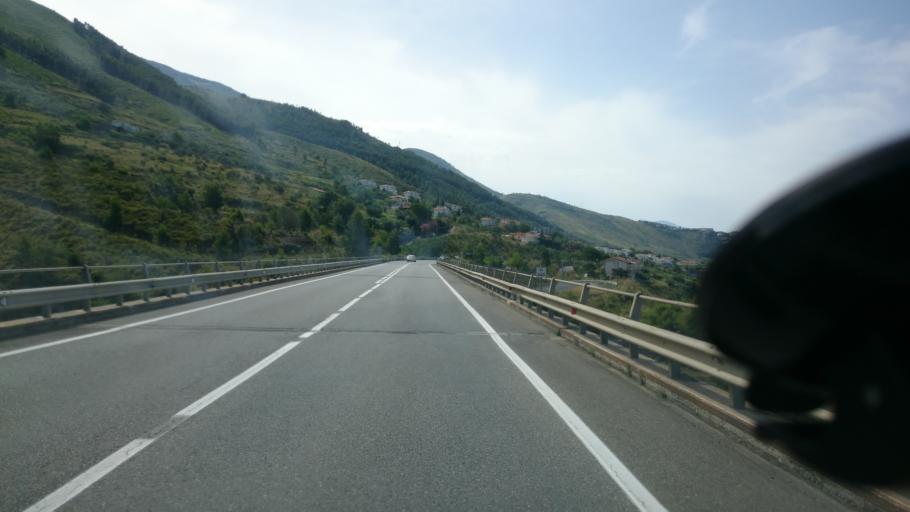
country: IT
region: Calabria
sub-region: Provincia di Cosenza
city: Praia a Mare
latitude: 39.8919
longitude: 15.7902
